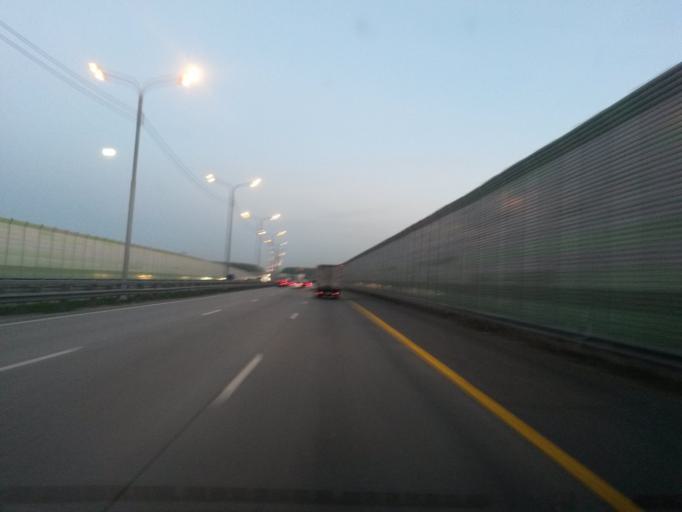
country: RU
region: Moskovskaya
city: Belyye Stolby
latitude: 55.3156
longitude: 37.8169
